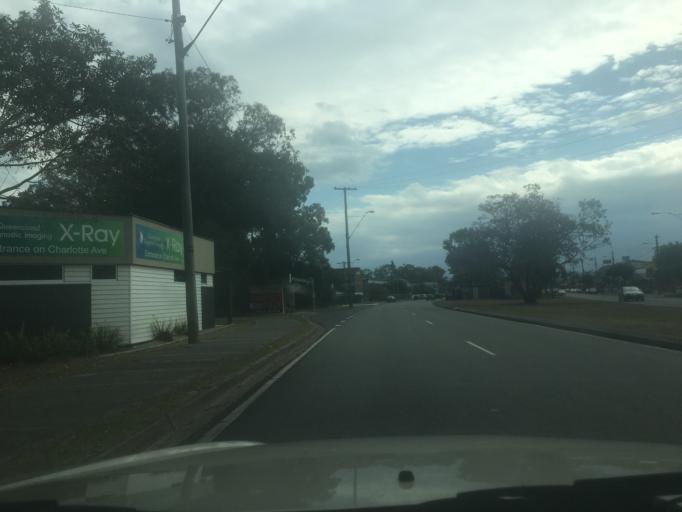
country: AU
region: Queensland
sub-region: Moreton Bay
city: Bongaree
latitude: -27.0651
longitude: 153.1532
